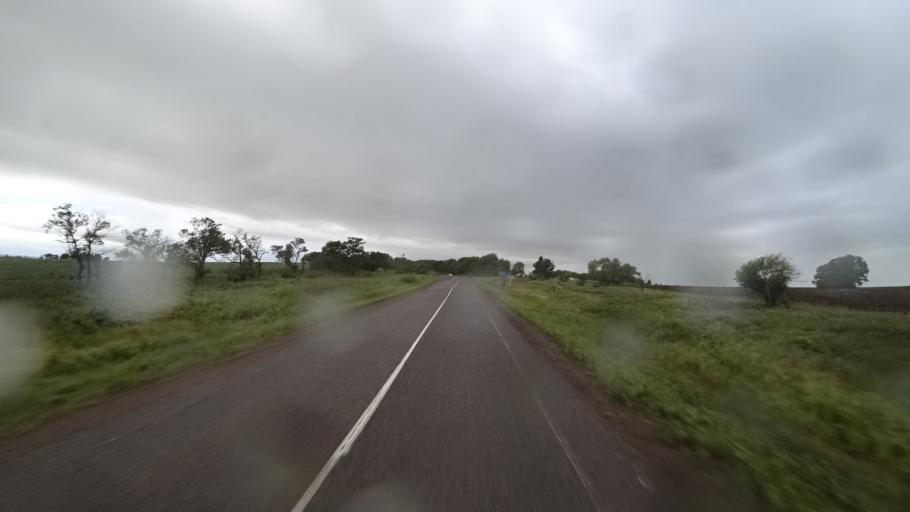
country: RU
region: Primorskiy
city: Chernigovka
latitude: 44.3661
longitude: 132.5365
